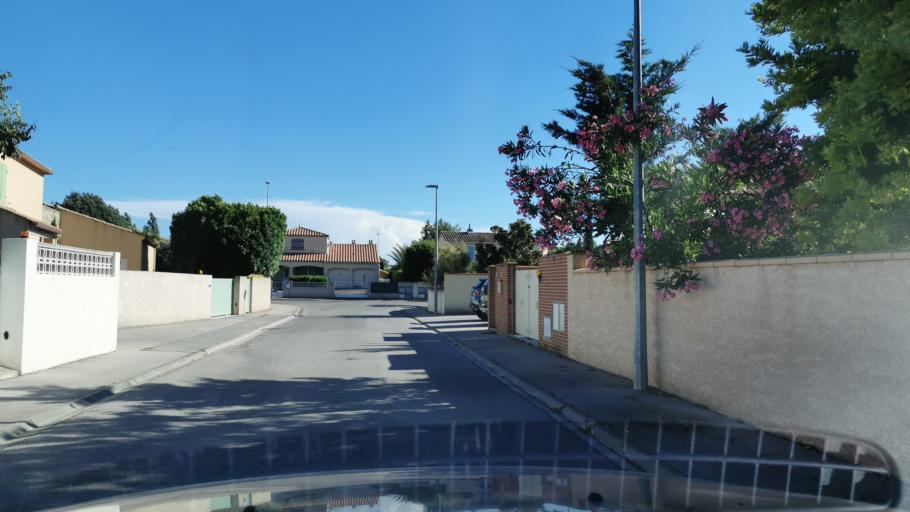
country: FR
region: Languedoc-Roussillon
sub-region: Departement de l'Aude
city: Narbonne
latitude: 43.1976
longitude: 3.0200
